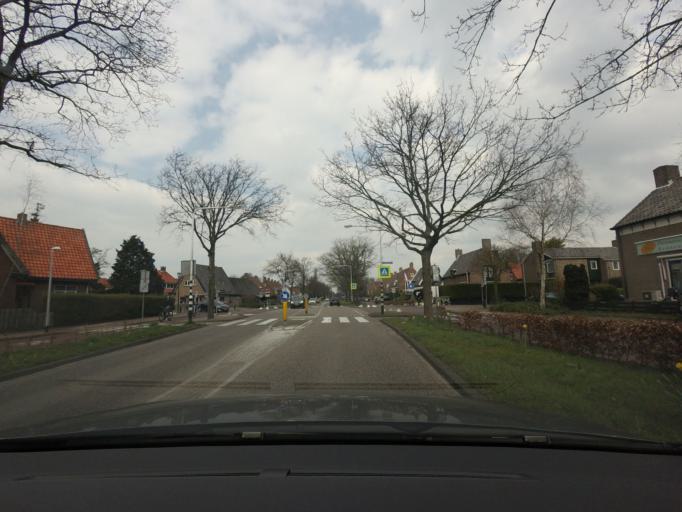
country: NL
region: North Holland
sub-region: Gemeente Alkmaar
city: Alkmaar
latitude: 52.6652
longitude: 4.7130
